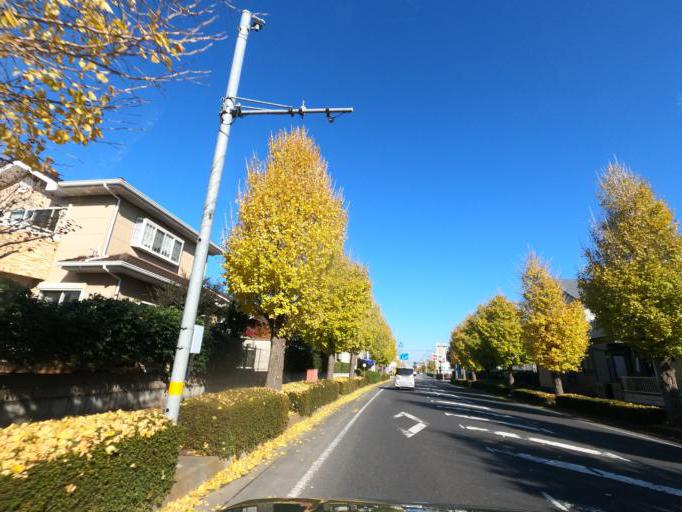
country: JP
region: Ibaraki
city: Mitsukaido
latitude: 35.9755
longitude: 139.9718
